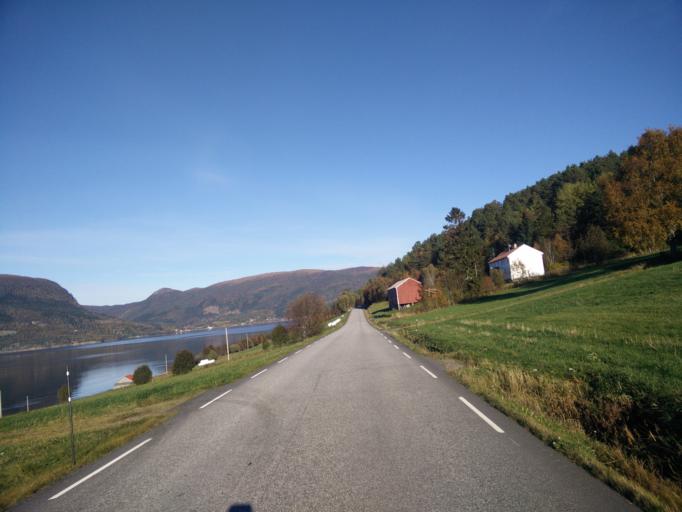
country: NO
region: More og Romsdal
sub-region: Halsa
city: Liaboen
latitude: 63.1344
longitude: 8.4076
